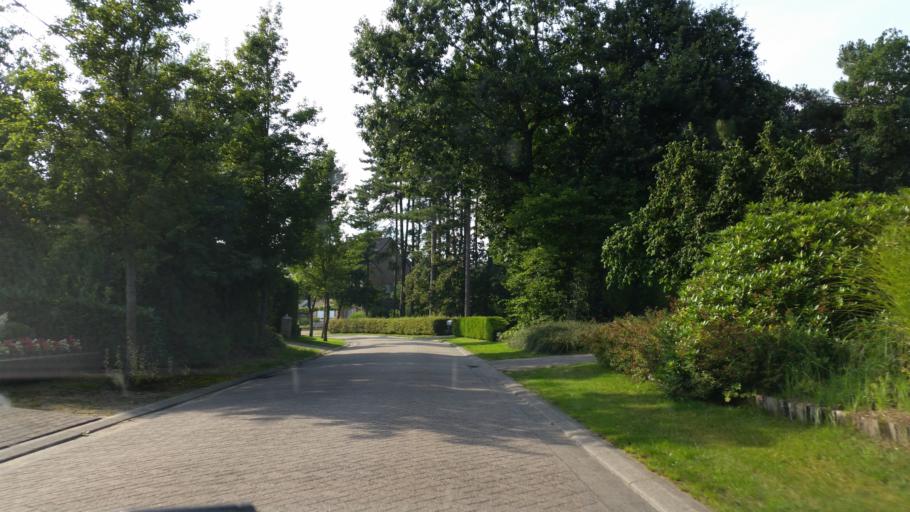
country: BE
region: Flanders
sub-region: Provincie Antwerpen
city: Kasterlee
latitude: 51.2293
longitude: 4.9296
